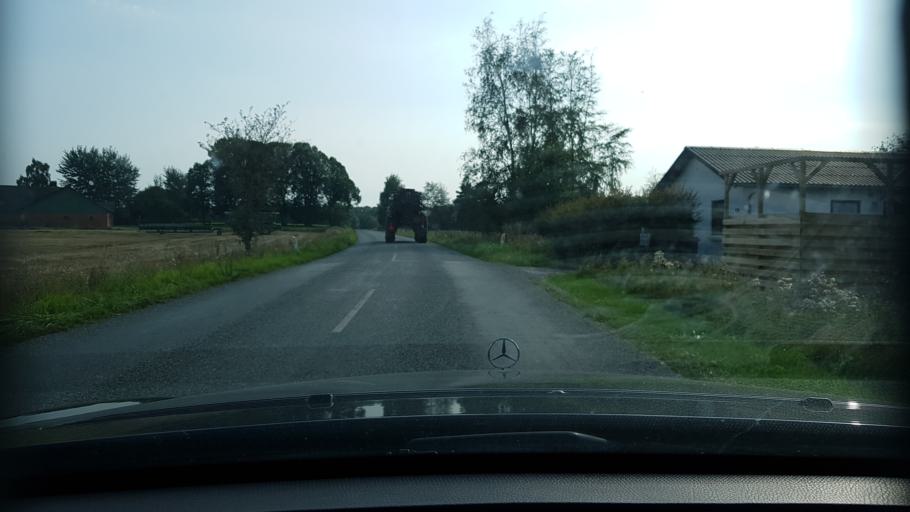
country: DK
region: North Denmark
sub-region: Mariagerfjord Kommune
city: Hadsund
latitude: 56.7564
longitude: 10.1856
